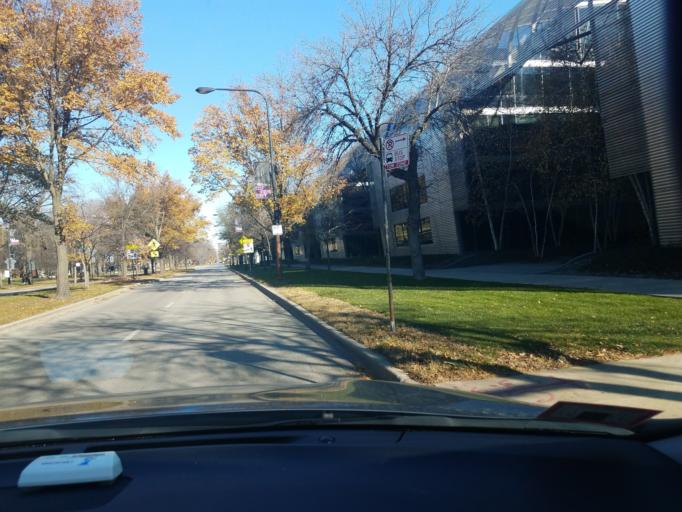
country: US
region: Illinois
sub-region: Cook County
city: Chicago
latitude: 41.8330
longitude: -87.6265
